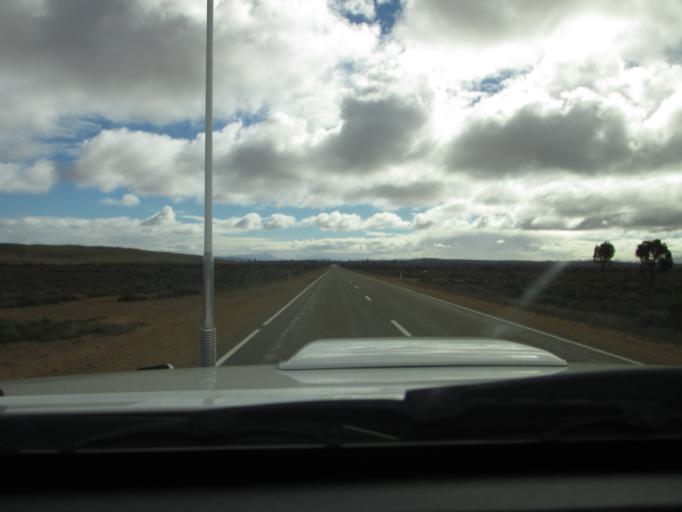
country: AU
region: South Australia
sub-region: Flinders Ranges
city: Quorn
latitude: -32.0957
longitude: 138.5025
